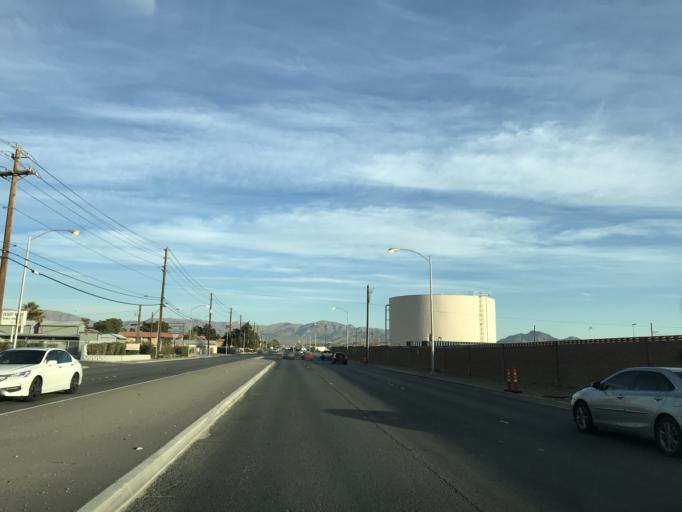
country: US
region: Nevada
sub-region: Clark County
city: Nellis Air Force Base
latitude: 36.2290
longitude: -115.0621
